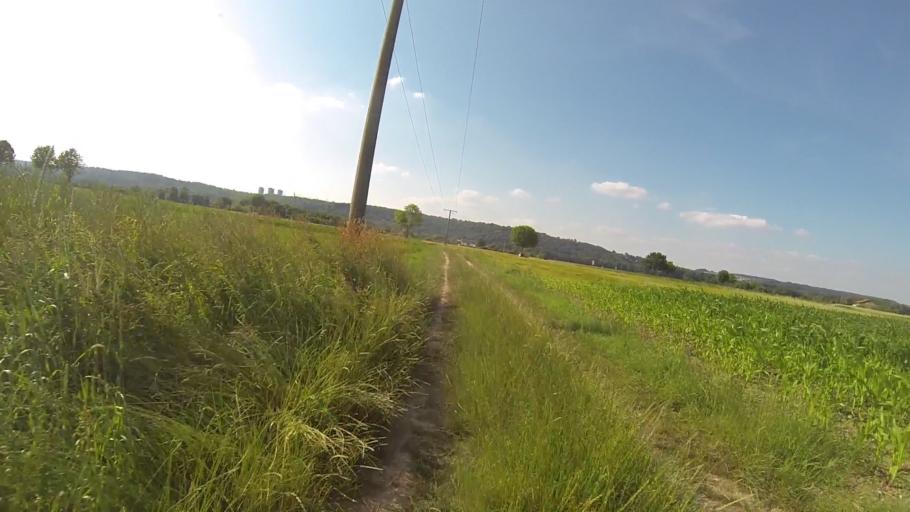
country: DE
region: Bavaria
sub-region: Swabia
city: Neu-Ulm
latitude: 48.4179
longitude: 10.0408
